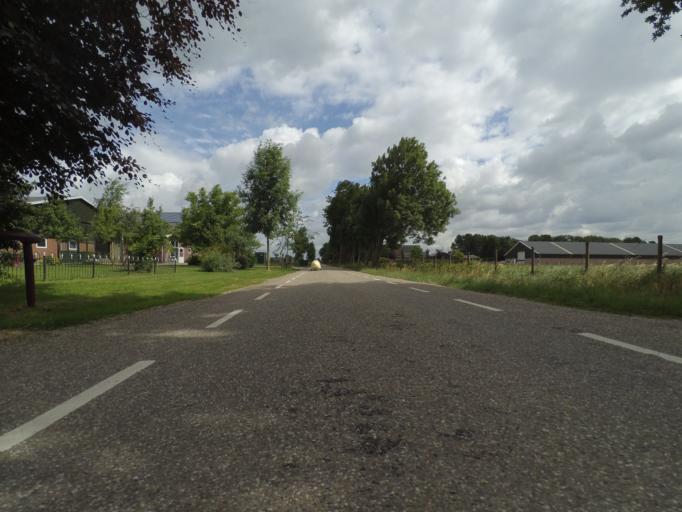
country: NL
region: Gelderland
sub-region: Gemeente Culemborg
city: Culemborg
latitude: 51.9958
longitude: 5.2497
